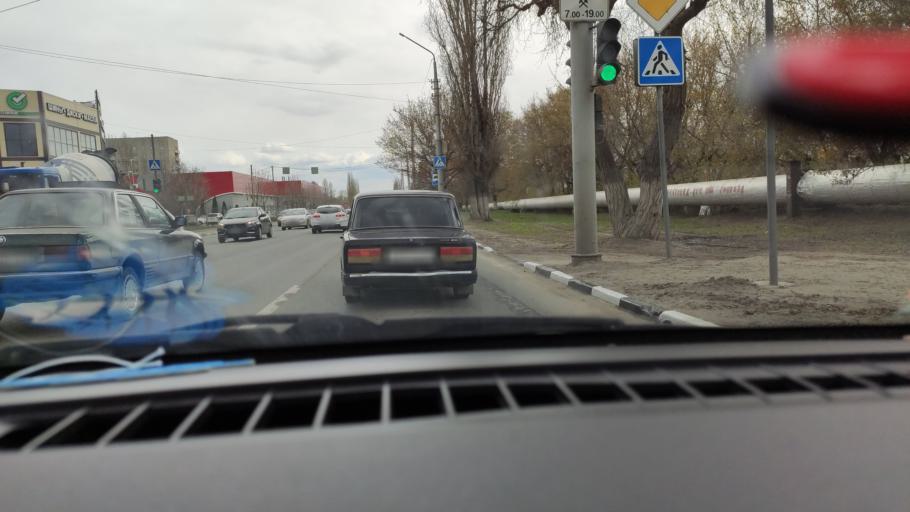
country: RU
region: Saratov
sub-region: Saratovskiy Rayon
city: Saratov
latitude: 51.5701
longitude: 45.9952
